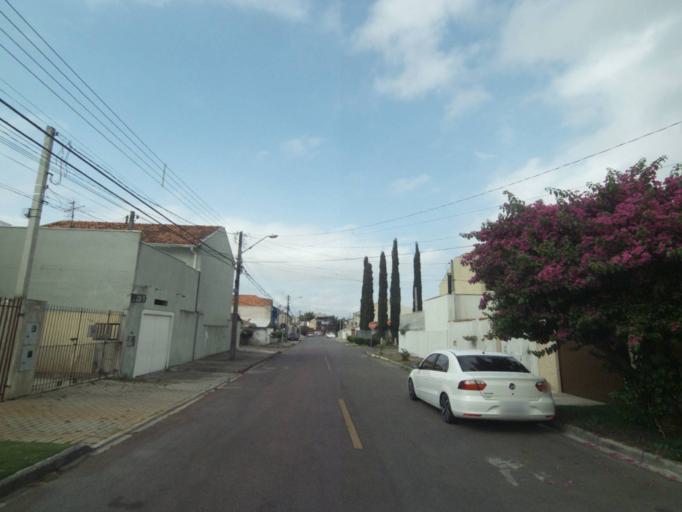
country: BR
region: Parana
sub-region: Sao Jose Dos Pinhais
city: Sao Jose dos Pinhais
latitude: -25.5389
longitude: -49.2577
